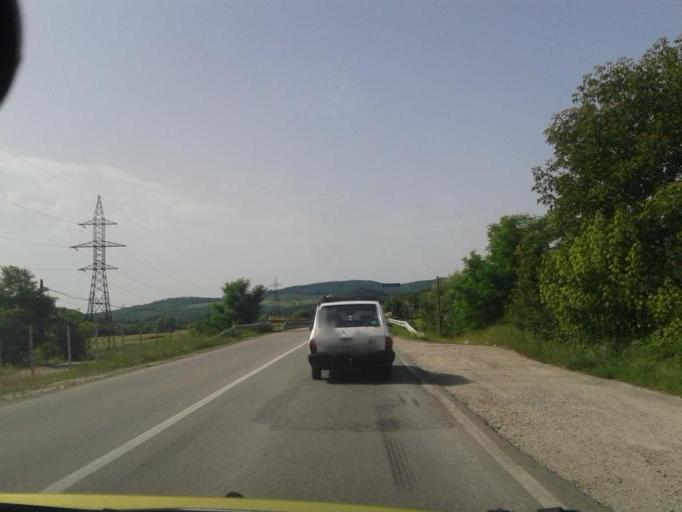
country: RO
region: Valcea
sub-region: Oras Baile Govora
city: Baile Govora
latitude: 45.0855
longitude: 24.2185
